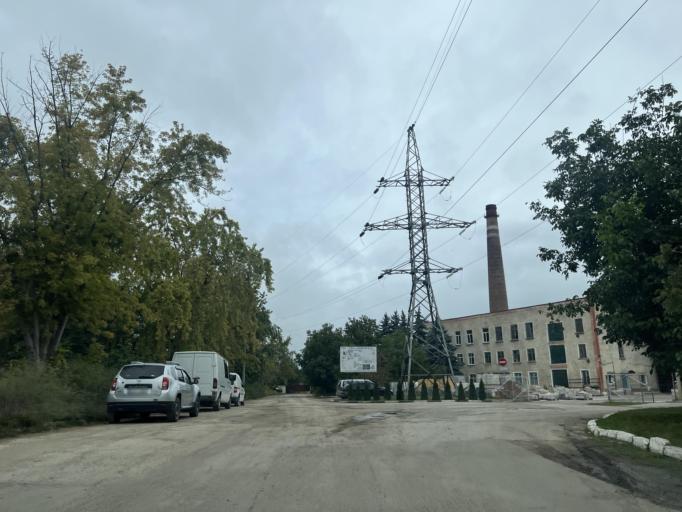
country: MD
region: Ungheni
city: Ungheni
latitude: 47.2258
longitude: 27.8052
